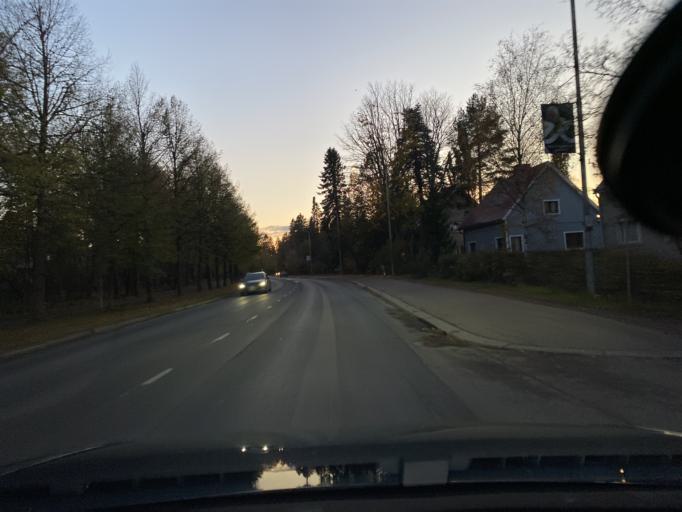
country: FI
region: Pirkanmaa
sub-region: Tampere
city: Tampere
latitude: 61.4728
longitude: 23.7579
